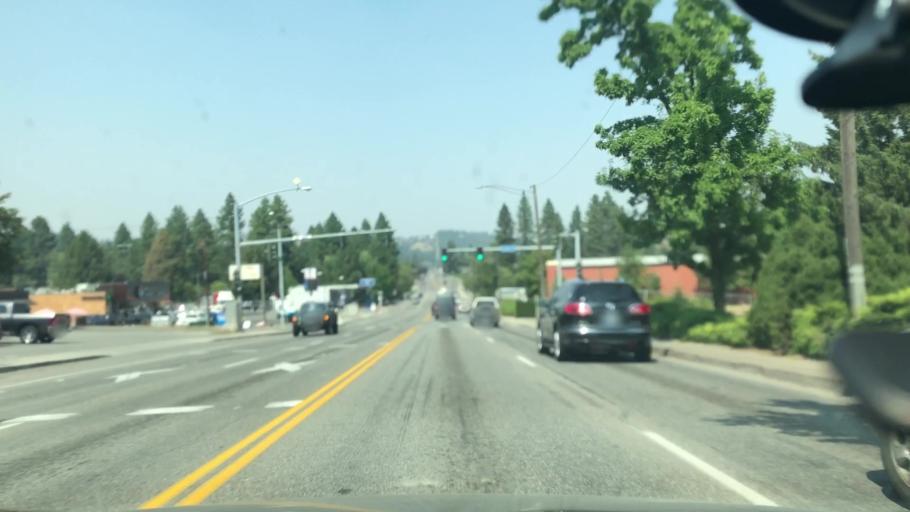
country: US
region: Washington
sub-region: Spokane County
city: Millwood
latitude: 47.6872
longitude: -117.2827
